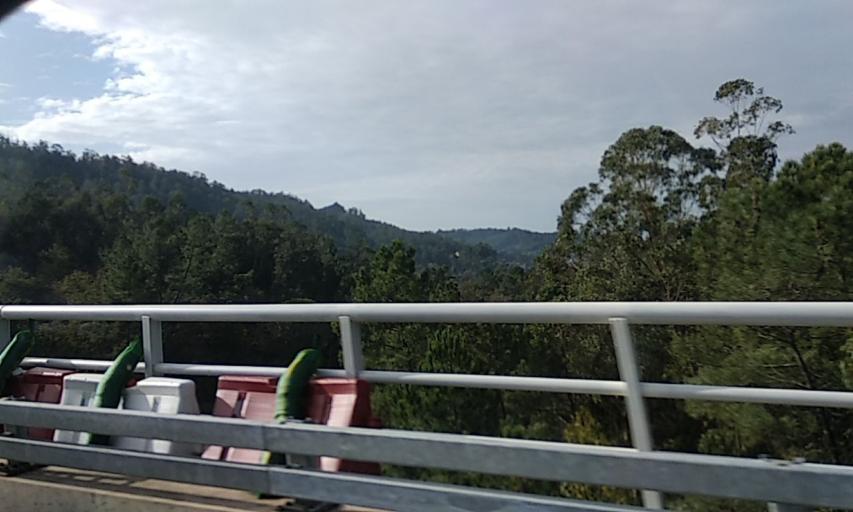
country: PT
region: Braga
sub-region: Braga
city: Oliveira
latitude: 41.4802
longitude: -8.4594
